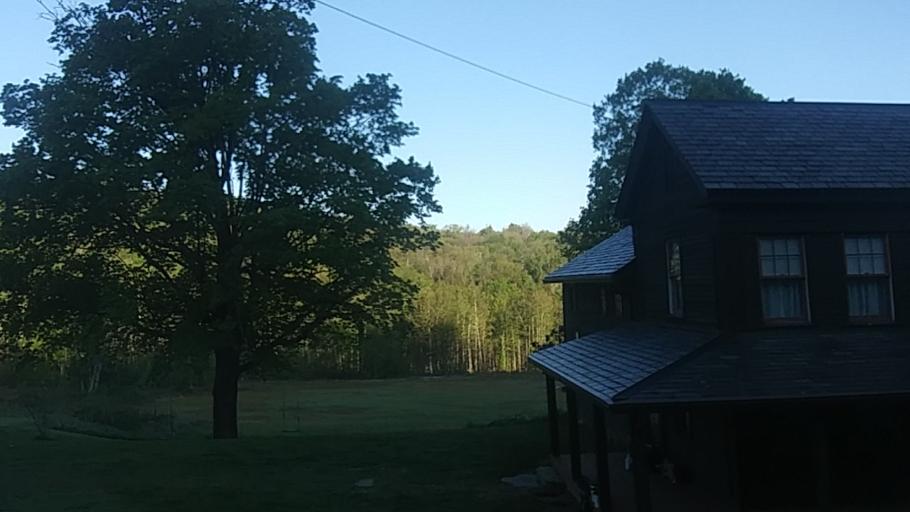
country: US
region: Massachusetts
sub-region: Franklin County
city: Shelburne Falls
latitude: 42.5988
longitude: -72.7598
